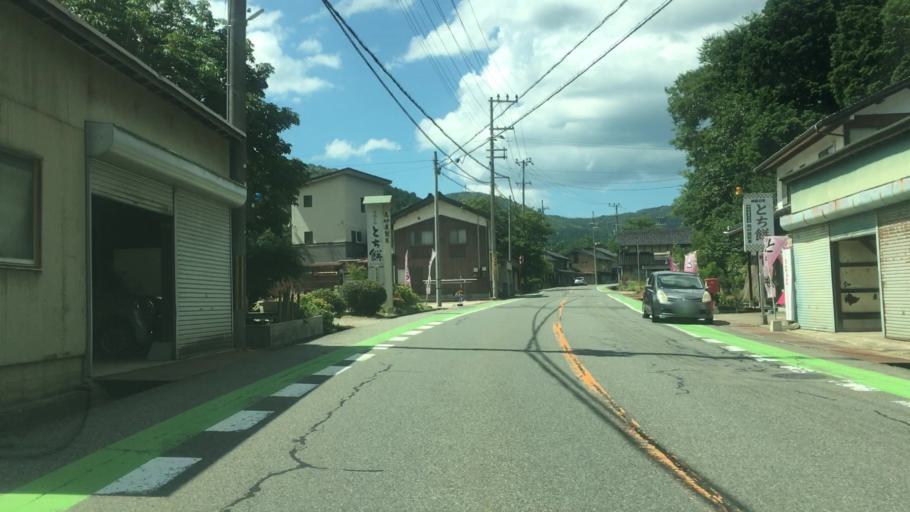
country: JP
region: Hyogo
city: Toyooka
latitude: 35.4773
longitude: 134.7095
